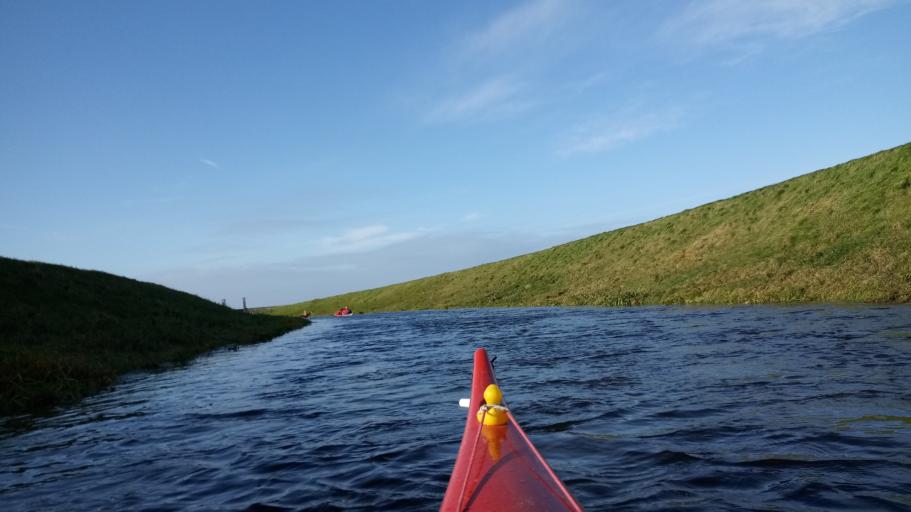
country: NL
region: Gelderland
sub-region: Gemeente Bronckhorst
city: Baak
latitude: 52.1001
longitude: 6.2239
